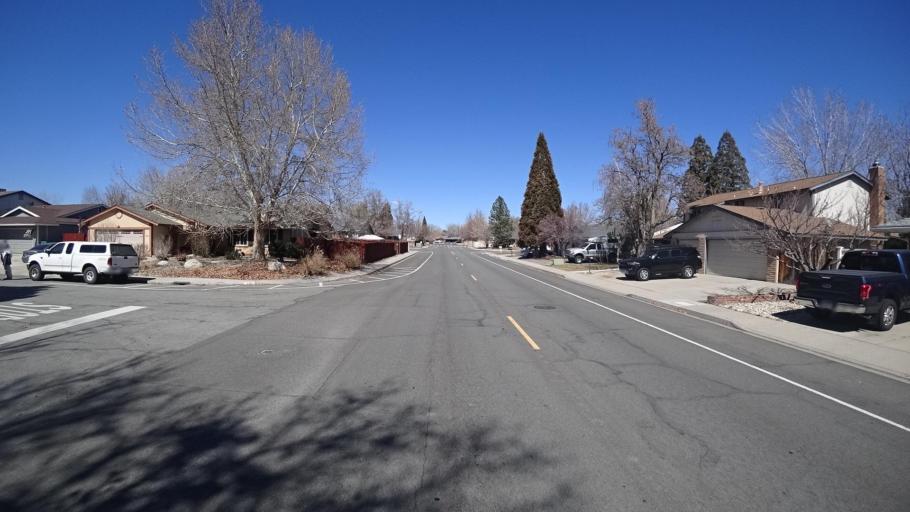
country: US
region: Nevada
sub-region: Washoe County
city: Sparks
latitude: 39.5551
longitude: -119.7156
